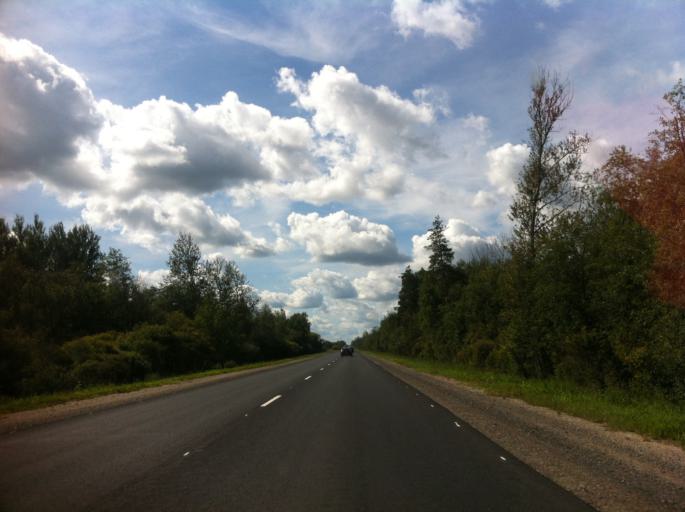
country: RU
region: Pskov
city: Izborsk
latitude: 57.7439
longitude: 28.0241
